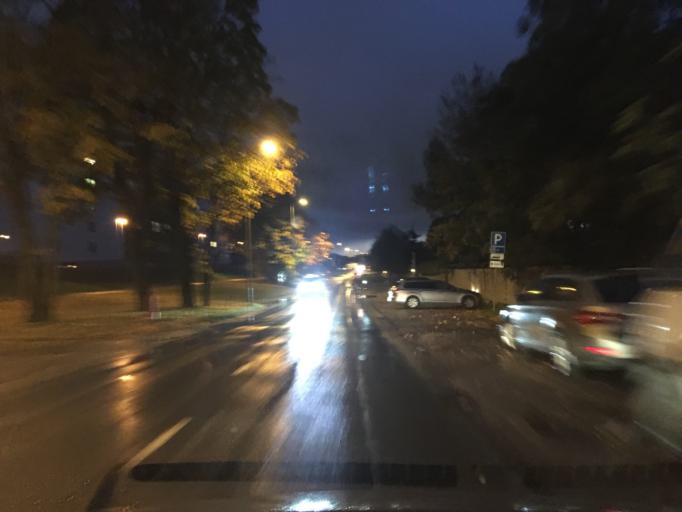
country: EE
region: Harju
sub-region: Tallinna linn
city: Tallinn
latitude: 59.4417
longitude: 24.8096
